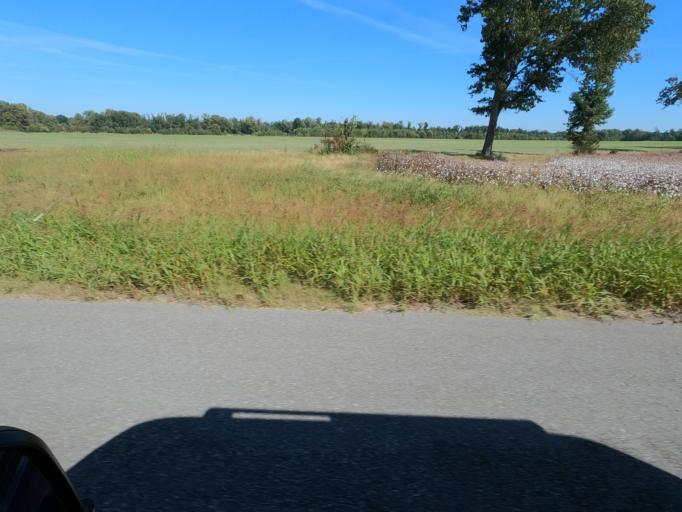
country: US
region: Tennessee
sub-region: Crockett County
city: Bells
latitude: 35.6896
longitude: -88.9937
